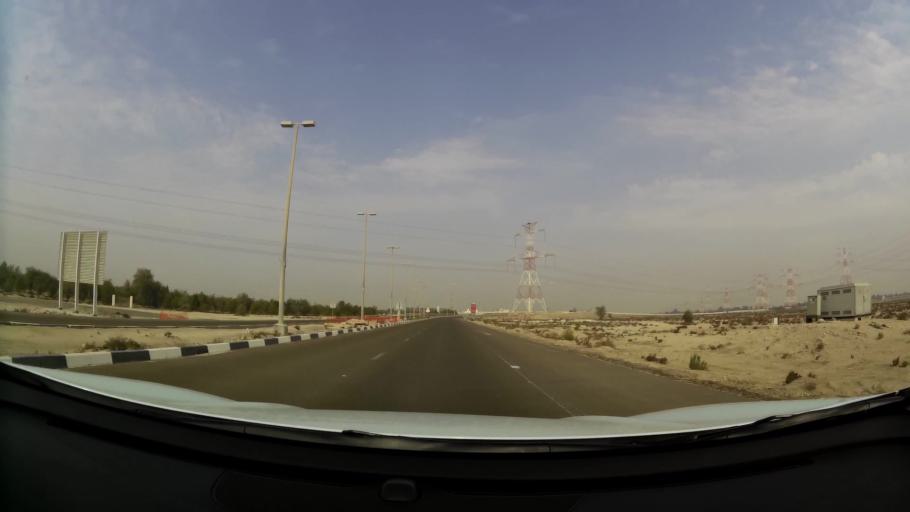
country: AE
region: Abu Dhabi
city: Abu Dhabi
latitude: 24.6497
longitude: 54.7530
